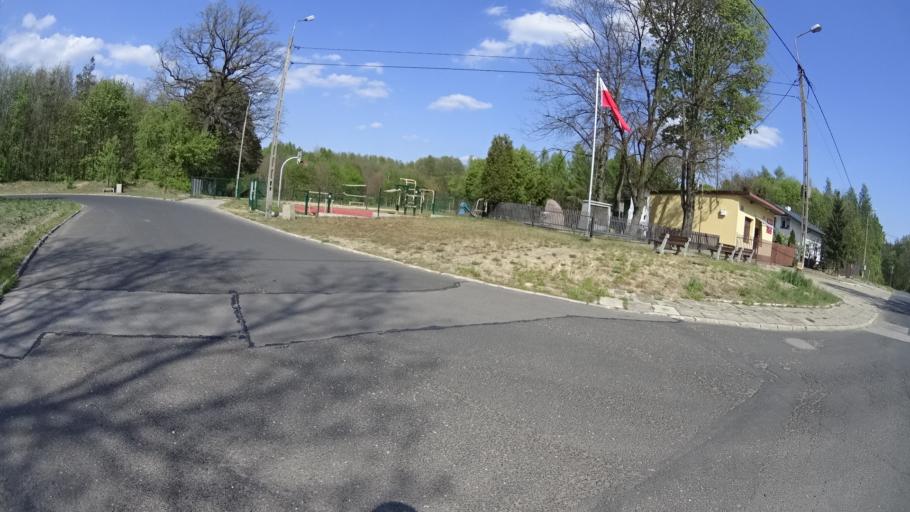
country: PL
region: Masovian Voivodeship
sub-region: Powiat warszawski zachodni
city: Izabelin
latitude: 52.3125
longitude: 20.8128
